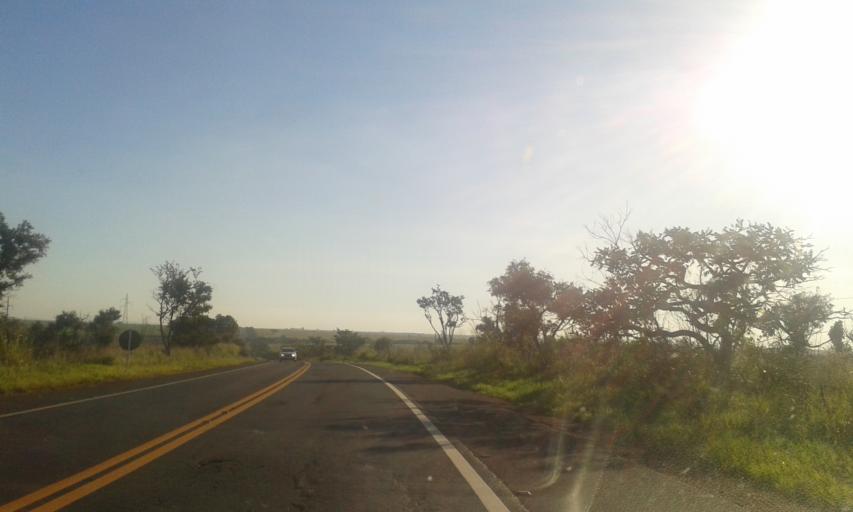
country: BR
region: Minas Gerais
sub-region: Ituiutaba
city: Ituiutaba
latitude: -18.8807
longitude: -49.1958
